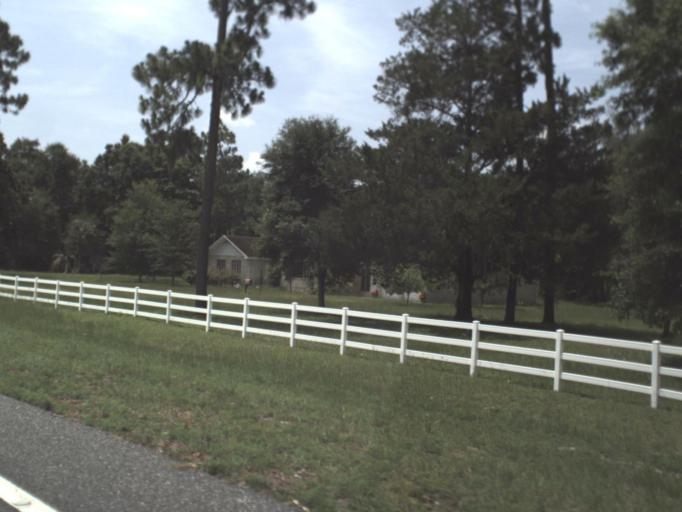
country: US
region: Florida
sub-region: Taylor County
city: Perry
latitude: 30.0418
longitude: -83.5490
